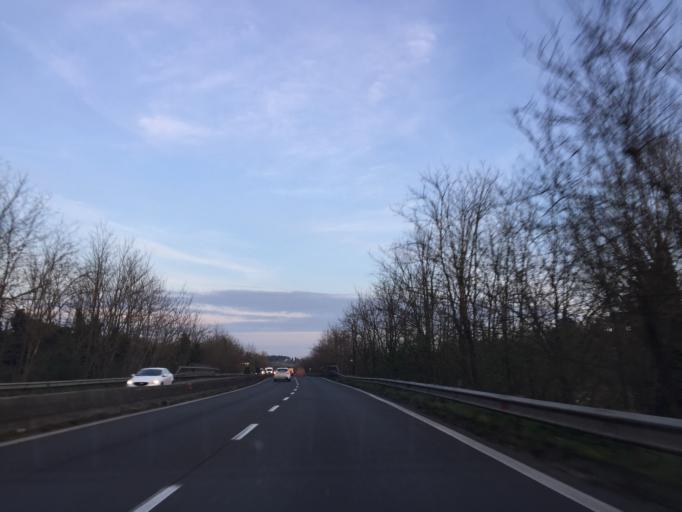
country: IT
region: Latium
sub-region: Citta metropolitana di Roma Capitale
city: Monte Caminetto
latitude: 41.9992
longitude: 12.4530
